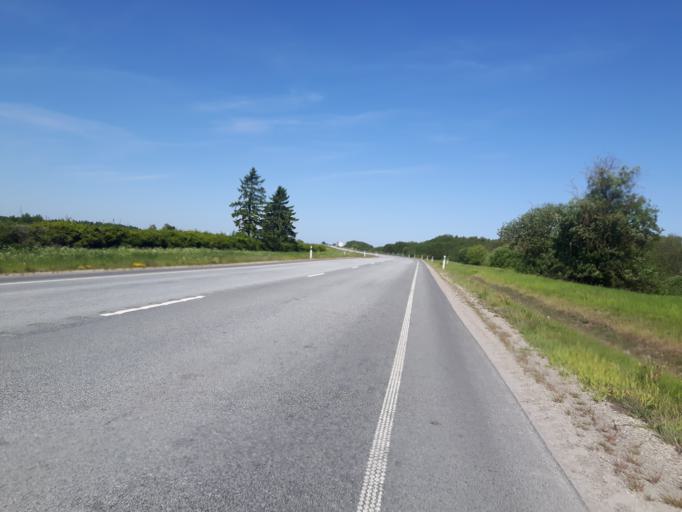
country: EE
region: Ida-Virumaa
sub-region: Kivioli linn
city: Kivioli
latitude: 59.4308
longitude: 26.9468
